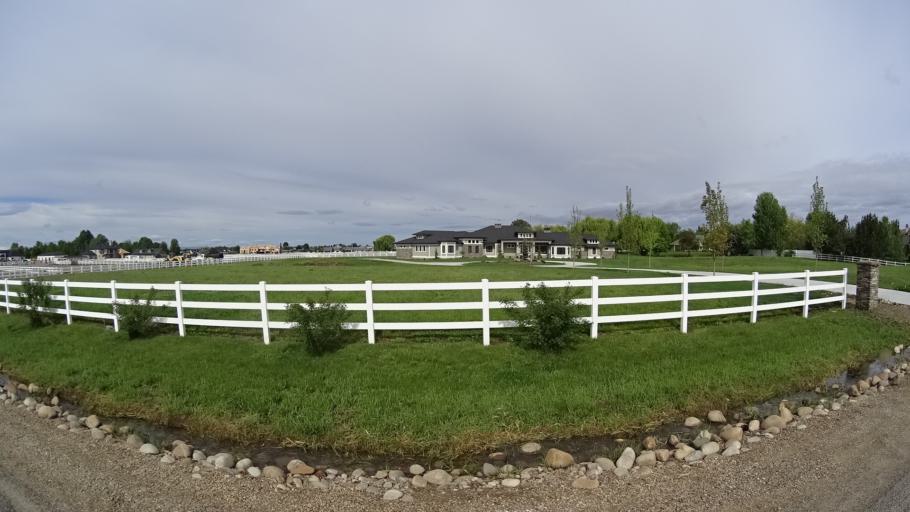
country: US
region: Idaho
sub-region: Ada County
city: Eagle
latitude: 43.7285
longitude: -116.4034
